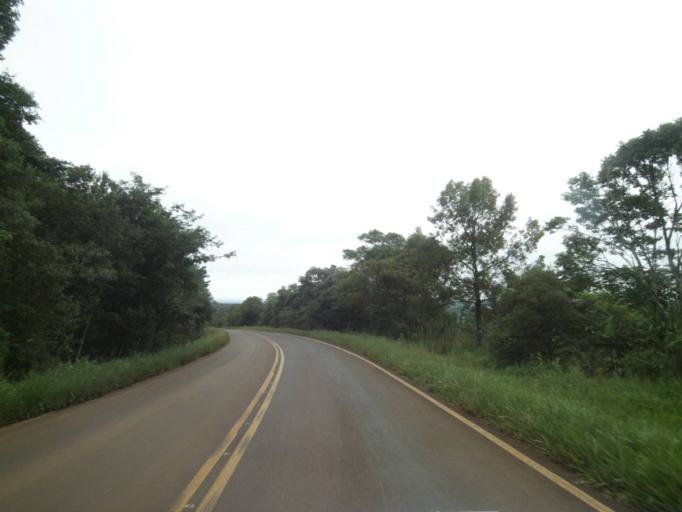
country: BR
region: Parana
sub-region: Pitanga
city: Pitanga
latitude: -24.9178
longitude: -51.8706
